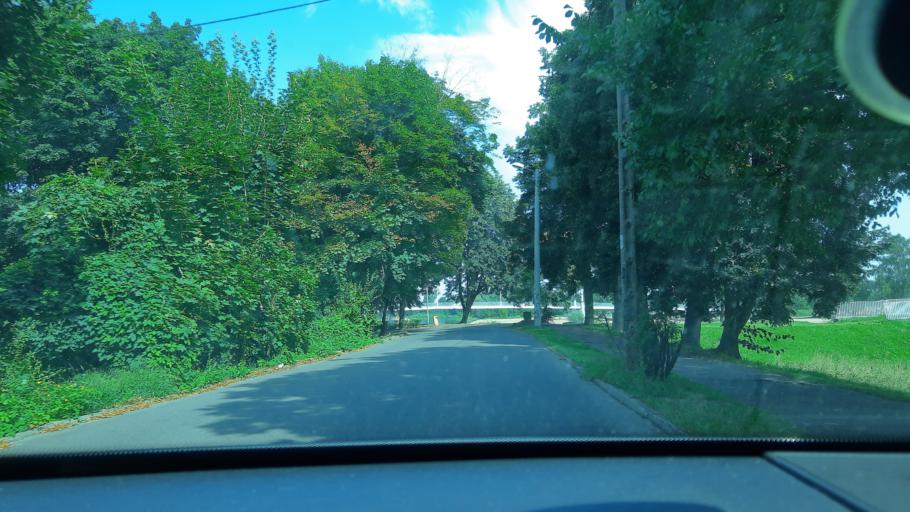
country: PL
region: Lodz Voivodeship
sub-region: Powiat sieradzki
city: Sieradz
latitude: 51.5989
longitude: 18.7425
